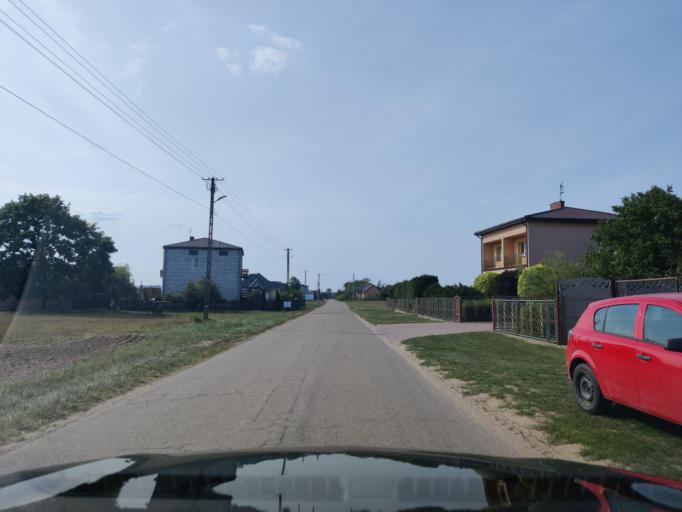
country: PL
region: Masovian Voivodeship
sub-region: Powiat pultuski
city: Obryte
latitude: 52.7623
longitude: 21.2970
